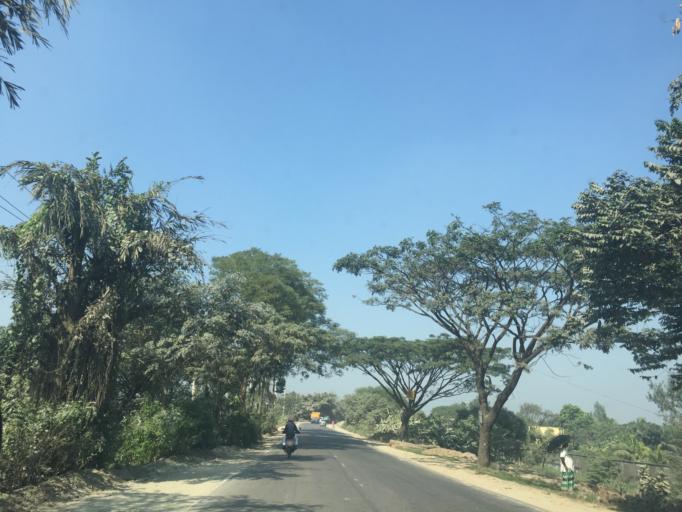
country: BD
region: Dhaka
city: Tungi
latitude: 23.8451
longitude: 90.3413
